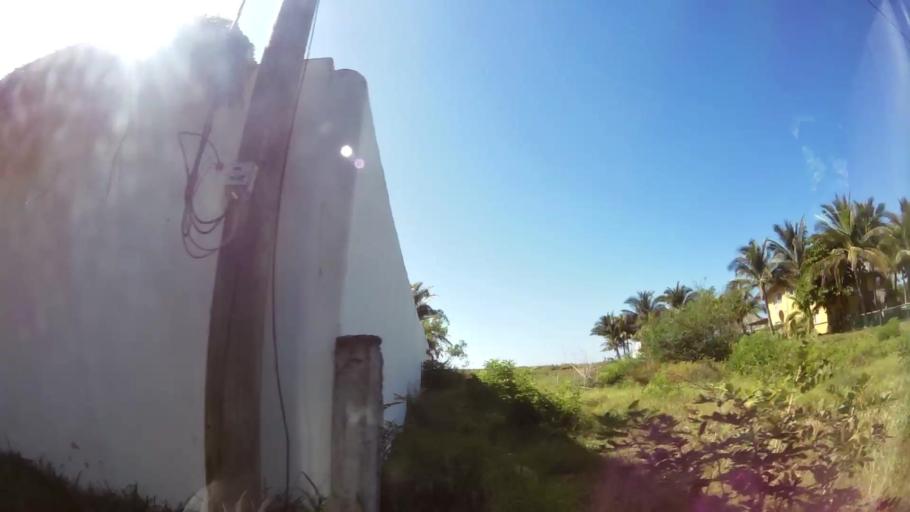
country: GT
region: Santa Rosa
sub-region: Municipio de Taxisco
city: Taxisco
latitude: 13.8810
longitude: -90.4545
